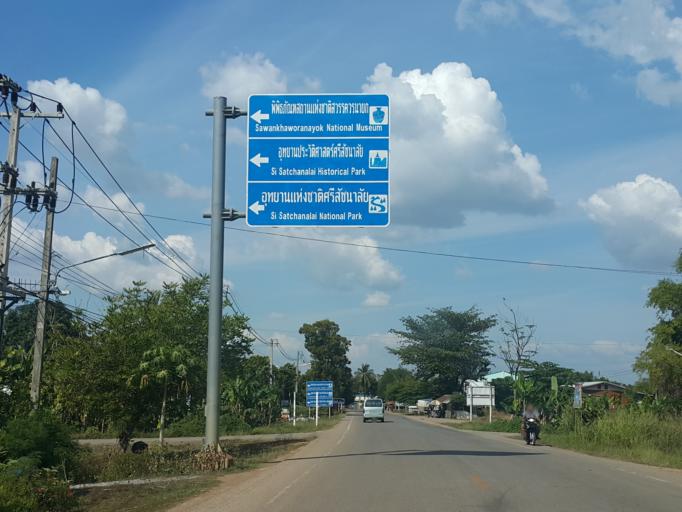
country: TH
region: Sukhothai
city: Sawankhalok
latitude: 17.2989
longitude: 99.8267
